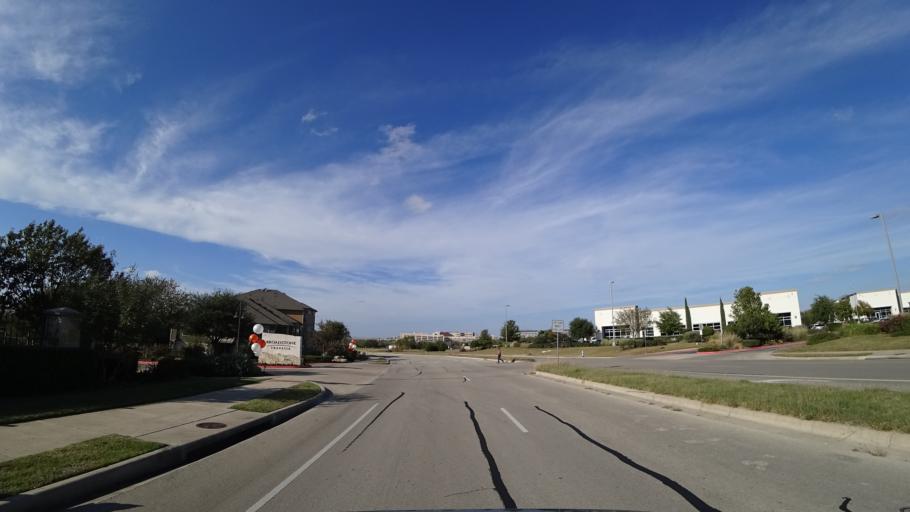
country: US
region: Texas
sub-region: Travis County
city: Wells Branch
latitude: 30.4698
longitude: -97.6882
